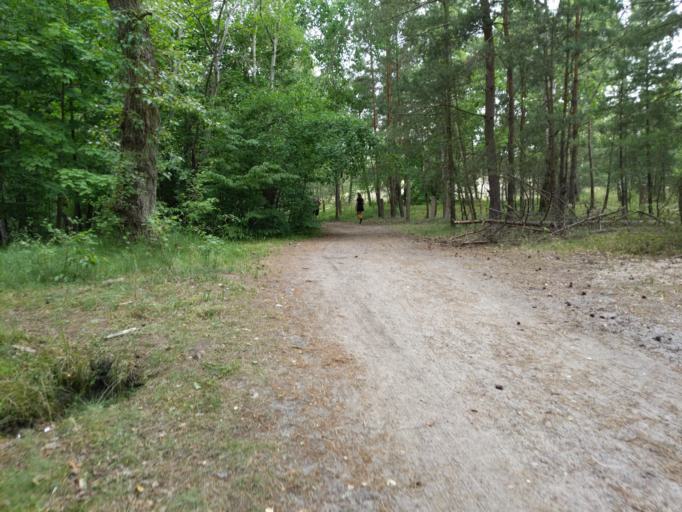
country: PL
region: Pomeranian Voivodeship
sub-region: Gdansk
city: Gdansk
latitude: 54.3709
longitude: 18.7356
